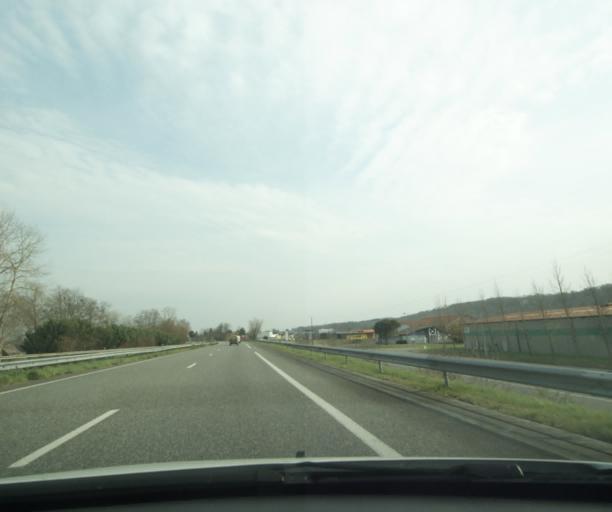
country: FR
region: Aquitaine
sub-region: Departement des Pyrenees-Atlantiques
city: Orthez
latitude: 43.4723
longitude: -0.7569
